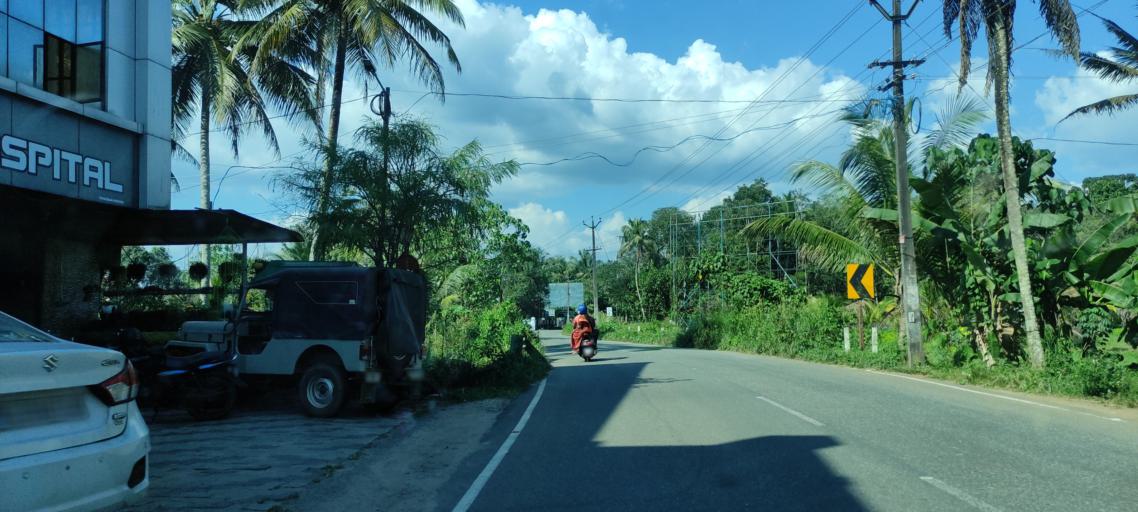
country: IN
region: Kerala
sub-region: Pattanamtitta
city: Adur
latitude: 9.2110
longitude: 76.7465
